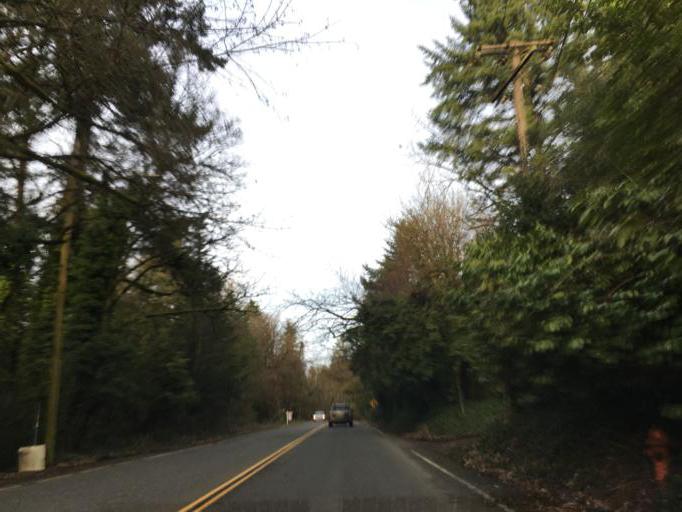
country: US
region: Oregon
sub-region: Clackamas County
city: Lake Oswego
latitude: 45.4507
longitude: -122.6851
